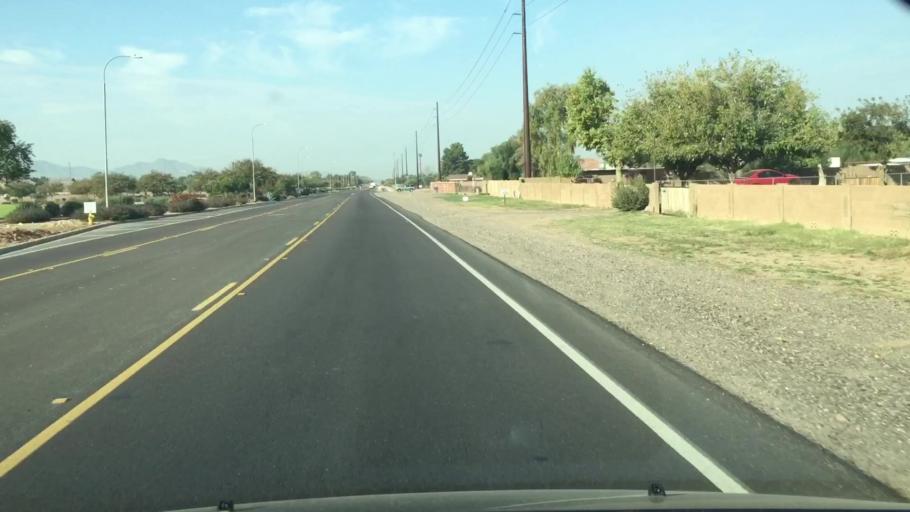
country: US
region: Arizona
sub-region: Maricopa County
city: Laveen
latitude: 33.3630
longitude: -112.1538
